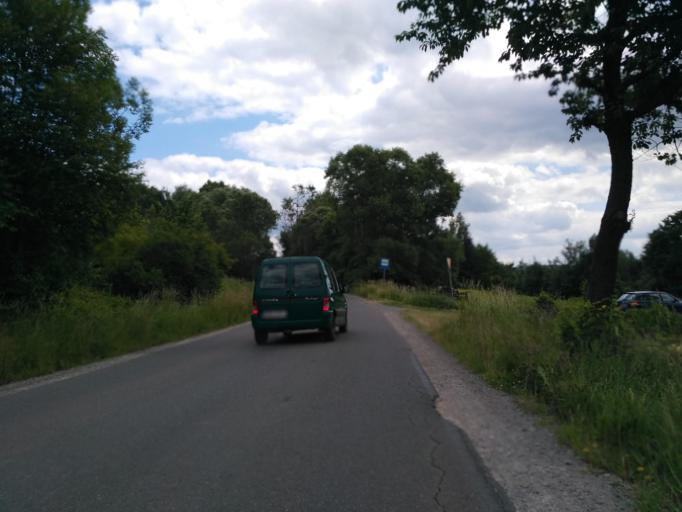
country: PL
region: Subcarpathian Voivodeship
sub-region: Powiat brzozowski
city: Nozdrzec
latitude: 49.7707
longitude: 22.2237
